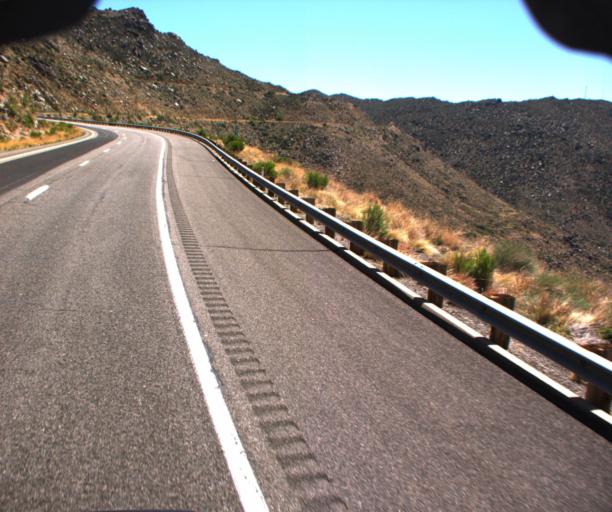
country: US
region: Arizona
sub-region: Yavapai County
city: Congress
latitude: 34.2022
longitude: -112.7757
